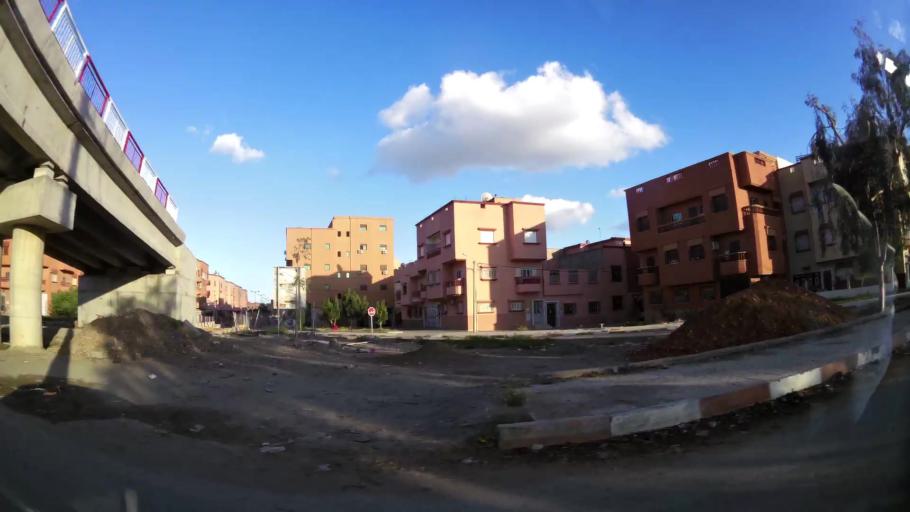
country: MA
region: Marrakech-Tensift-Al Haouz
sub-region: Kelaa-Des-Sraghna
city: Sidi Abdallah
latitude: 32.2410
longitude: -7.9628
